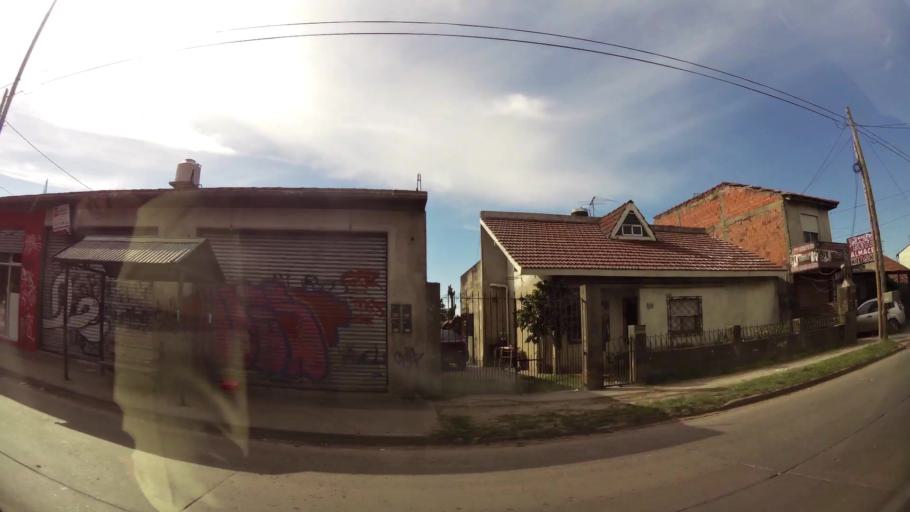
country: AR
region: Buenos Aires
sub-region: Partido de Almirante Brown
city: Adrogue
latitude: -34.8155
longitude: -58.3558
